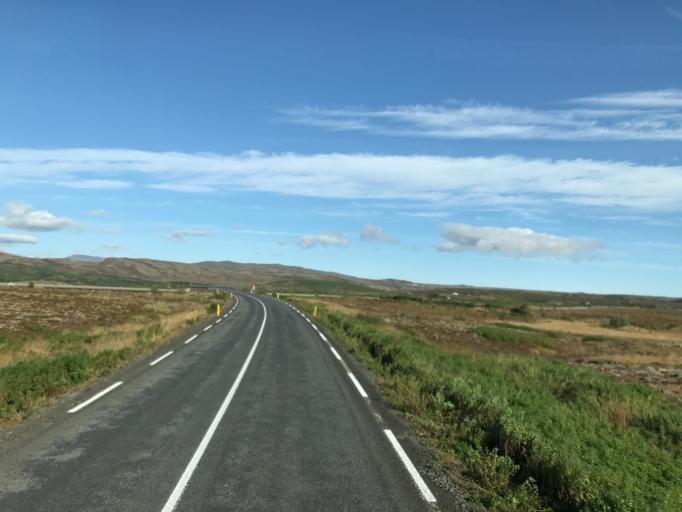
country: IS
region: Capital Region
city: Mosfellsbaer
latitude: 64.1081
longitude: -21.6714
